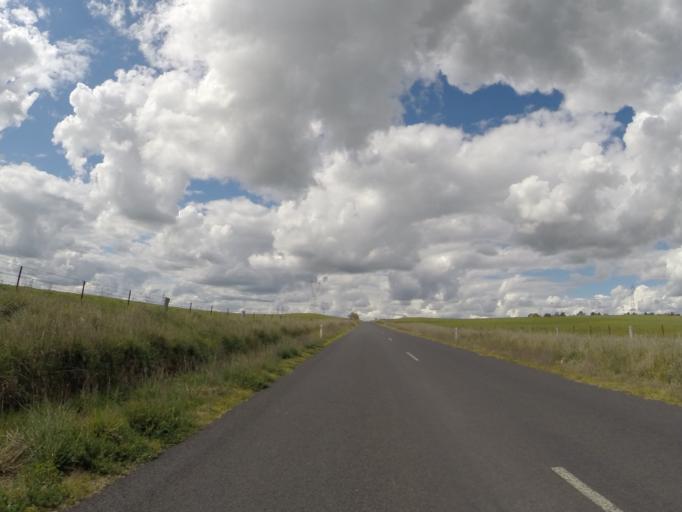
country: AU
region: New South Wales
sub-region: Yass Valley
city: Yass
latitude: -34.8766
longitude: 148.9017
